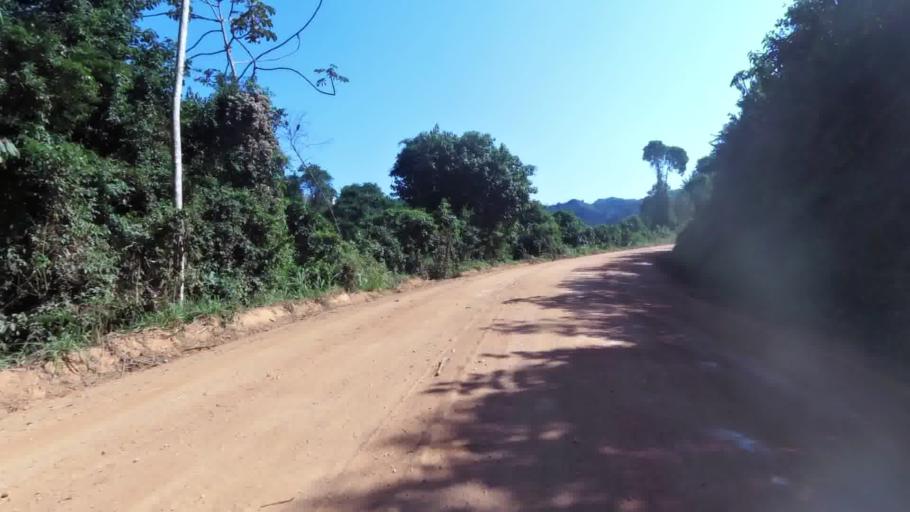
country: BR
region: Espirito Santo
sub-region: Alfredo Chaves
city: Alfredo Chaves
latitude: -20.5377
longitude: -40.8355
